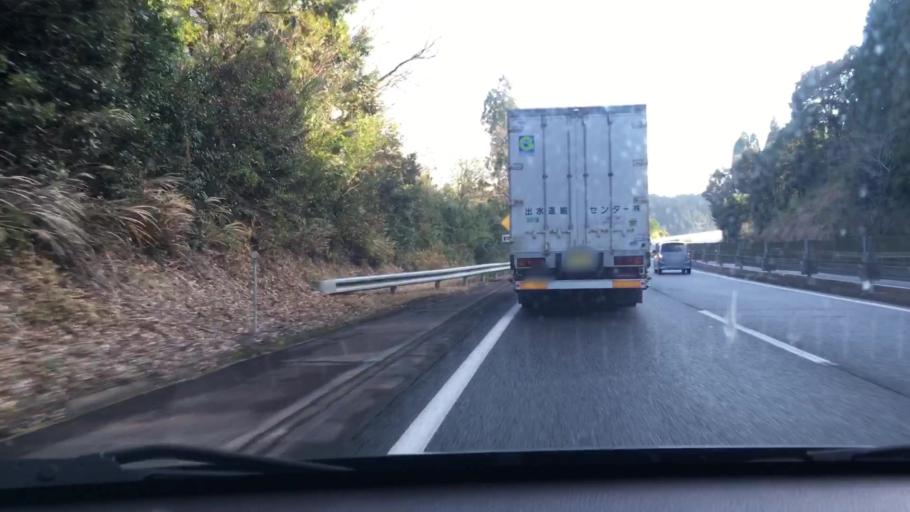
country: JP
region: Kagoshima
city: Kajiki
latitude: 31.9075
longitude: 130.7072
